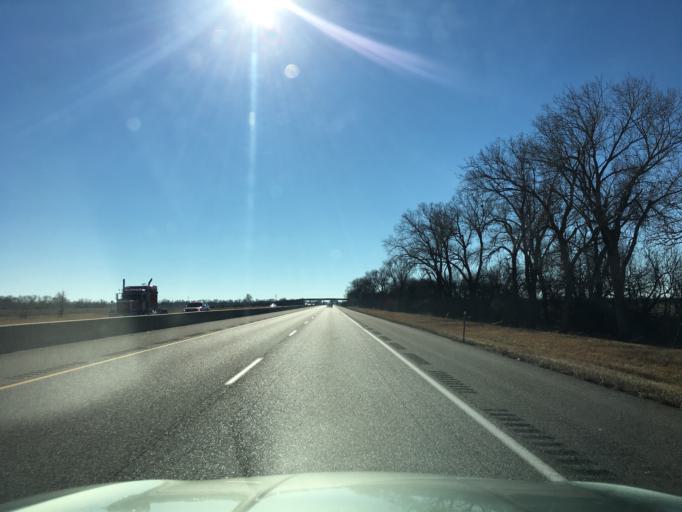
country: US
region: Kansas
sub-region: Sumner County
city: Belle Plaine
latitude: 37.4413
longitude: -97.3218
